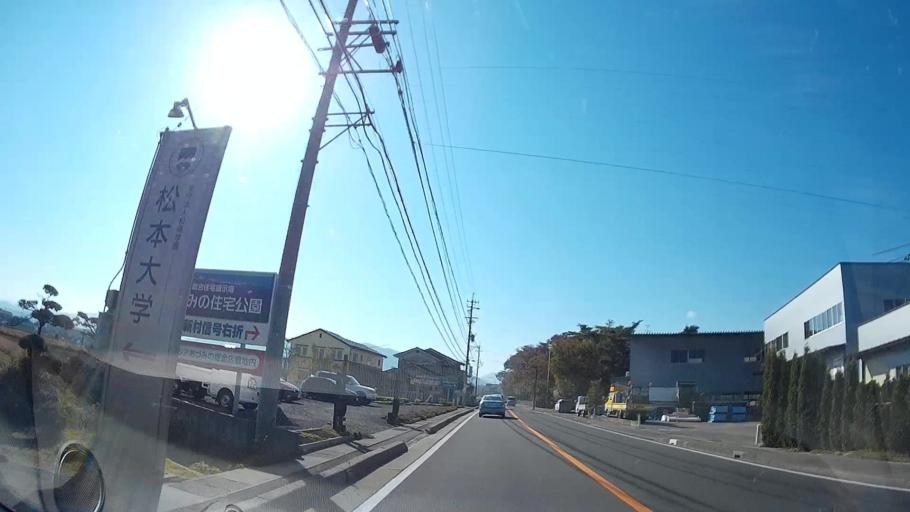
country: JP
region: Nagano
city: Matsumoto
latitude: 36.2216
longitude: 137.9085
